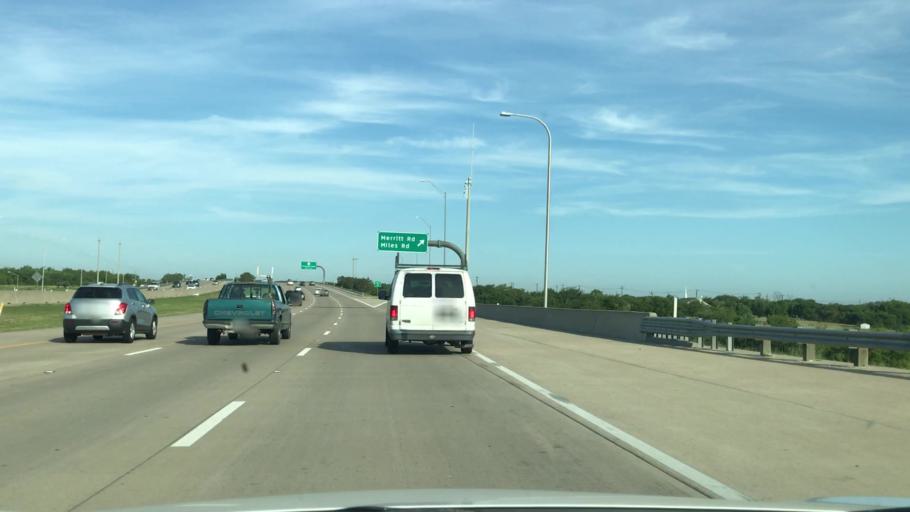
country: US
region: Texas
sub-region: Dallas County
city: Sachse
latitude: 32.9493
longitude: -96.5657
